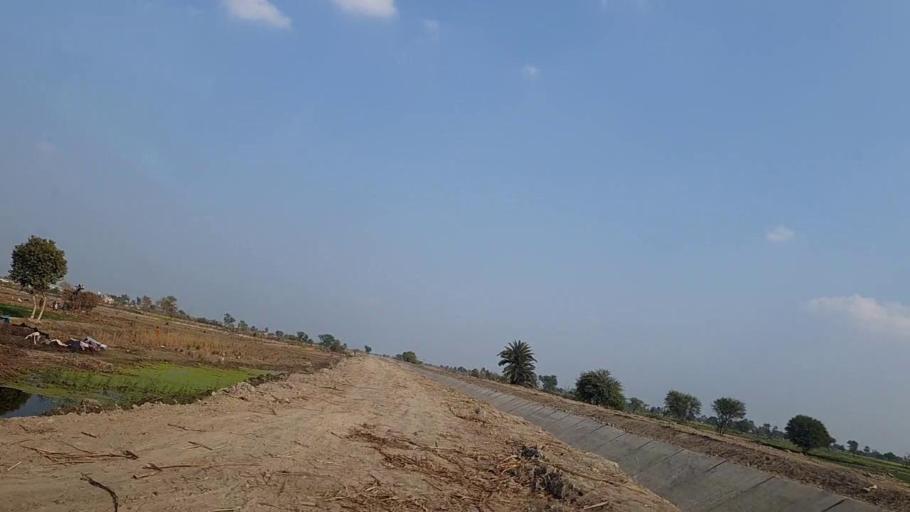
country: PK
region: Sindh
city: Nawabshah
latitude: 26.1485
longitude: 68.3833
